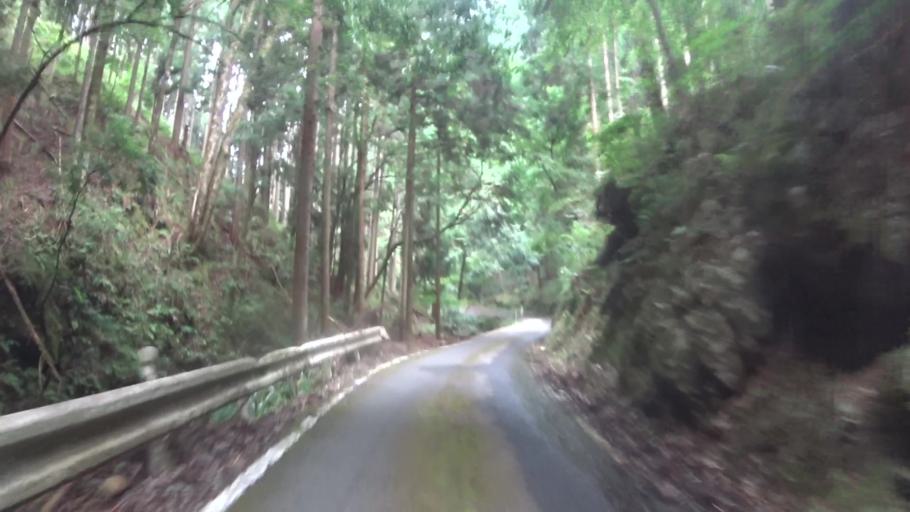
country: JP
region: Kyoto
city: Kameoka
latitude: 35.1545
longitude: 135.5738
